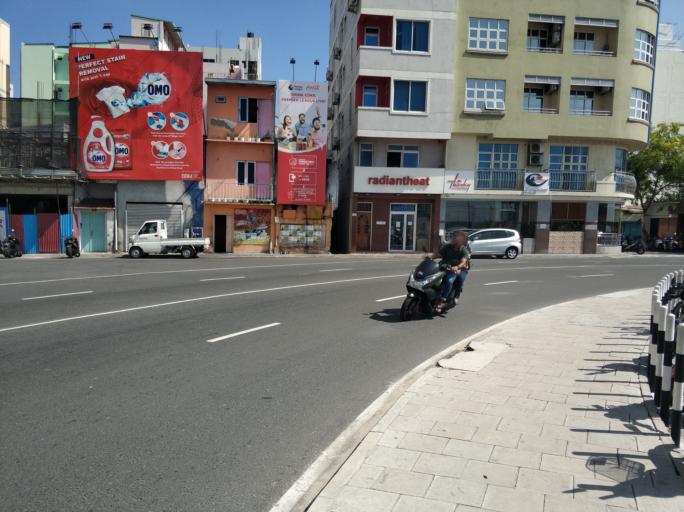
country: MV
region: Maale
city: Male
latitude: 4.1724
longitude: 73.5168
